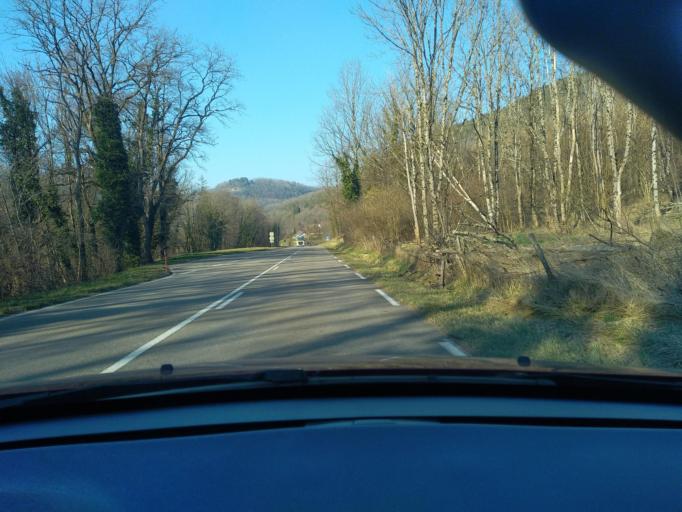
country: FR
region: Franche-Comte
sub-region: Departement du Jura
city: Perrigny
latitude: 46.6432
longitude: 5.6020
